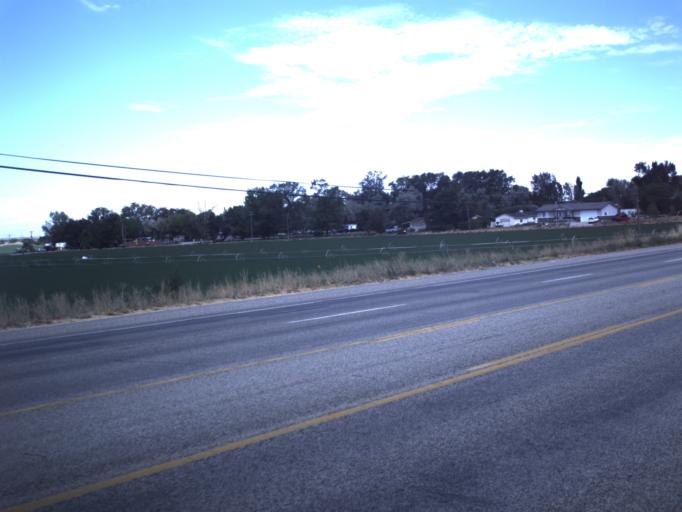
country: US
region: Utah
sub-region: Box Elder County
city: Perry
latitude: 41.4428
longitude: -112.0370
